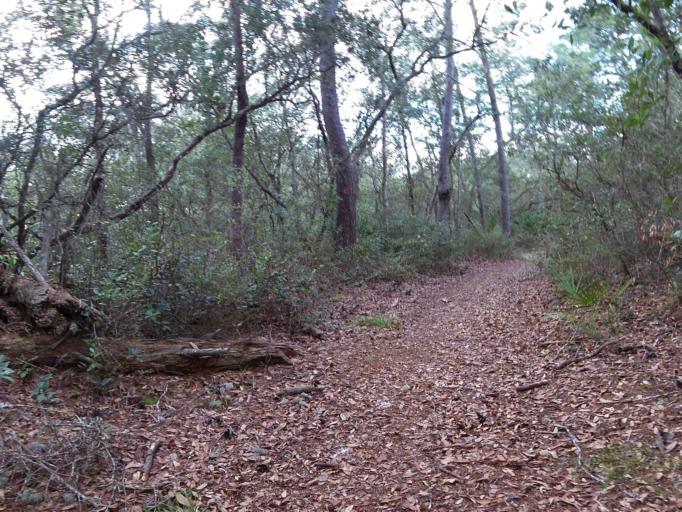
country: US
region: Florida
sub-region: Putnam County
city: Interlachen
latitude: 29.7544
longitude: -81.8173
